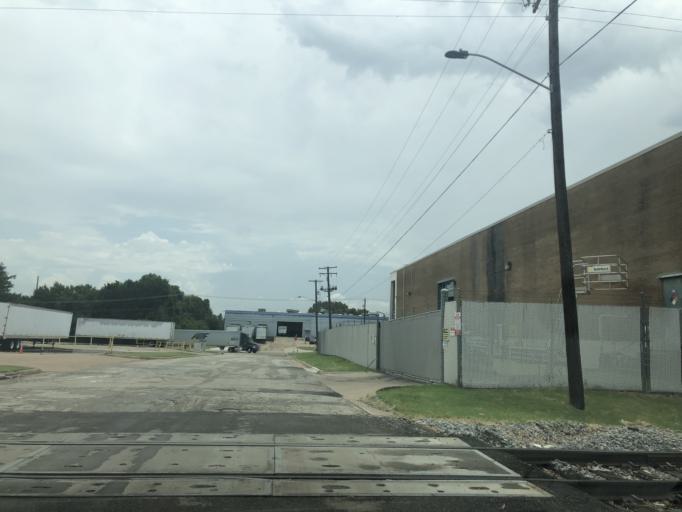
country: US
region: Texas
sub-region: Dallas County
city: Grand Prairie
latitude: 32.7576
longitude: -97.0440
